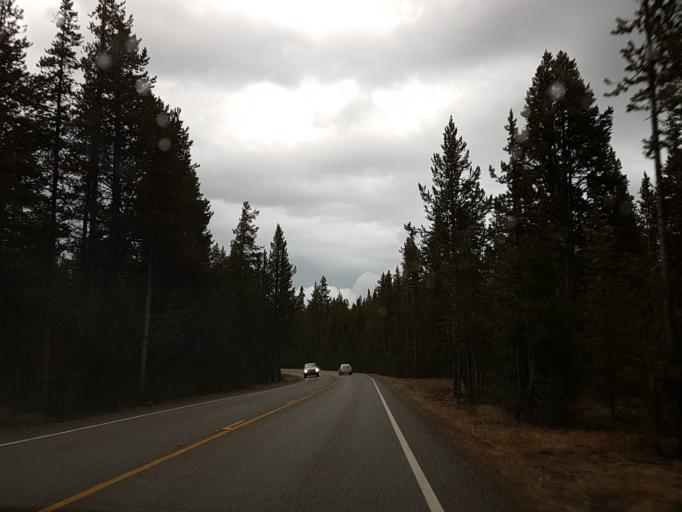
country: US
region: Montana
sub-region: Gallatin County
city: West Yellowstone
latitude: 44.4586
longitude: -110.5090
